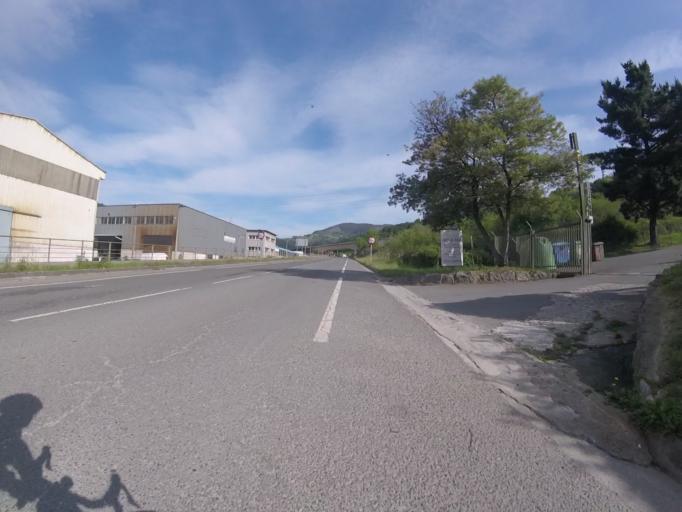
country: ES
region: Basque Country
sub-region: Provincia de Guipuzcoa
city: Gabiria
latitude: 43.0723
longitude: -2.2879
